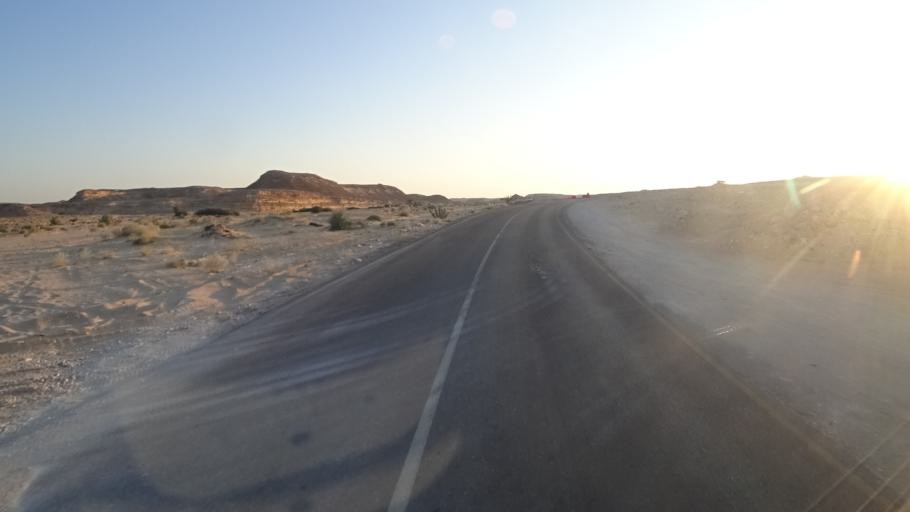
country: OM
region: Zufar
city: Salalah
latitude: 17.5165
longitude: 53.3745
